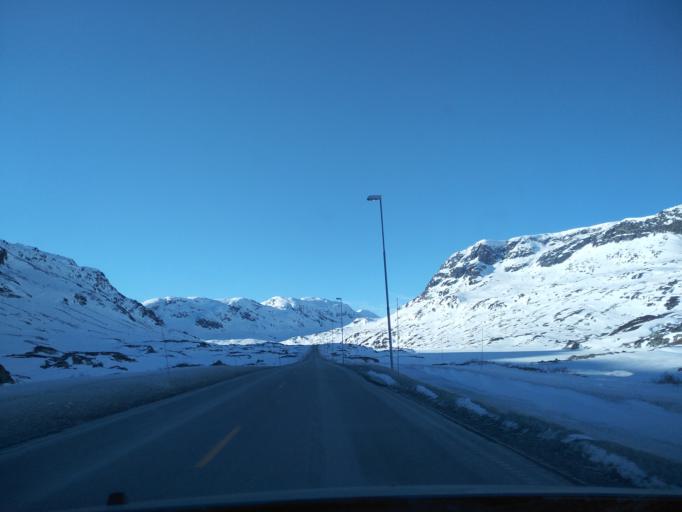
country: NO
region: Aust-Agder
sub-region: Bykle
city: Hovden
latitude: 59.8486
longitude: 7.1258
